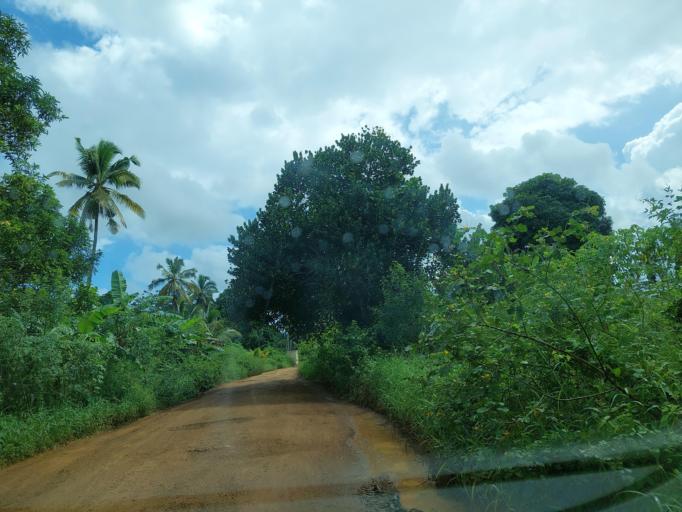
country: YT
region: M'Tsangamouji
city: M'Tsangamouji
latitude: -12.7505
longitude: 45.1171
